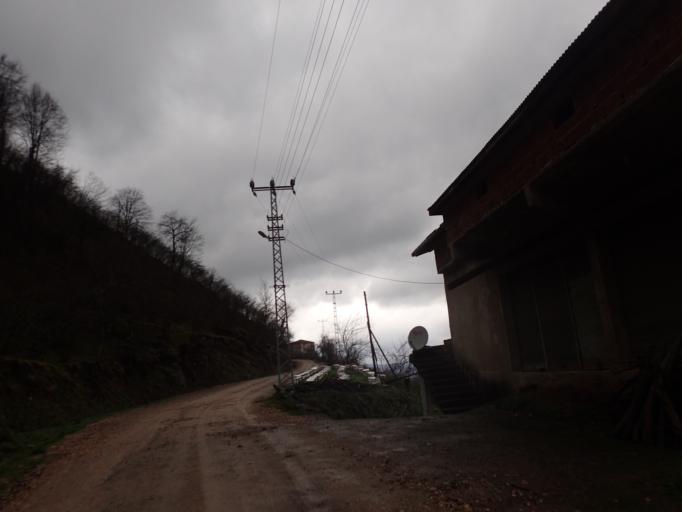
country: TR
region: Ordu
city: Camas
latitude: 40.8685
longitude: 37.5062
